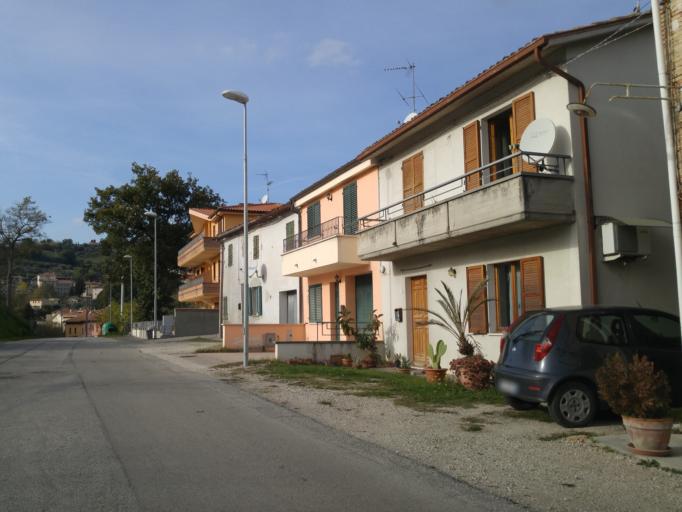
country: IT
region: The Marches
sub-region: Provincia di Pesaro e Urbino
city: Saltara
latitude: 43.7512
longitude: 12.9038
